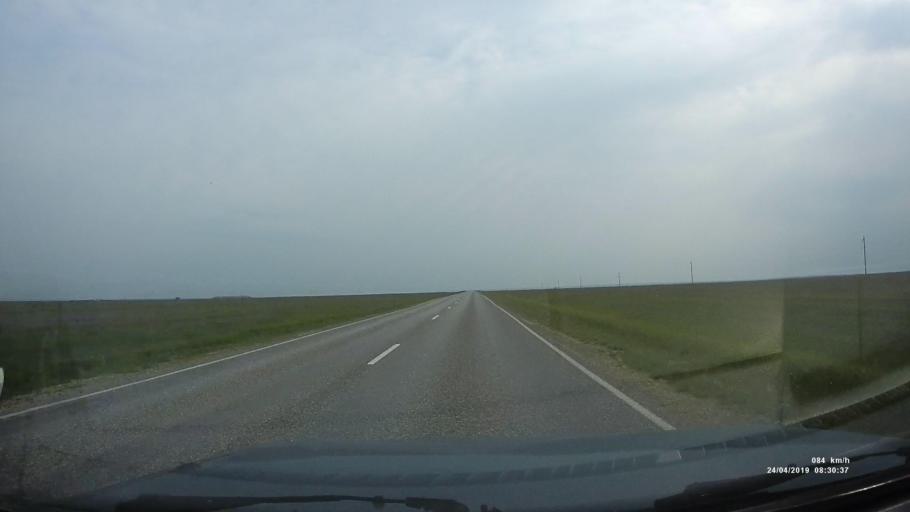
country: RU
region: Kalmykiya
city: Priyutnoye
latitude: 46.1608
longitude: 43.8482
